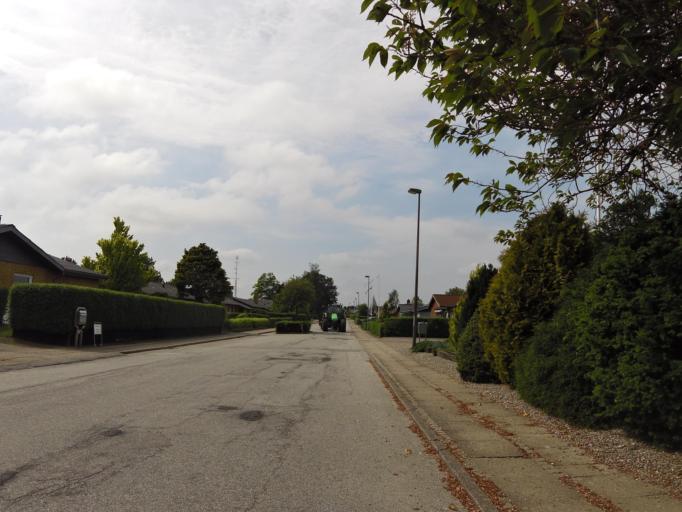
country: DK
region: South Denmark
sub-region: Haderslev Kommune
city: Vojens
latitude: 55.2723
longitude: 9.1796
